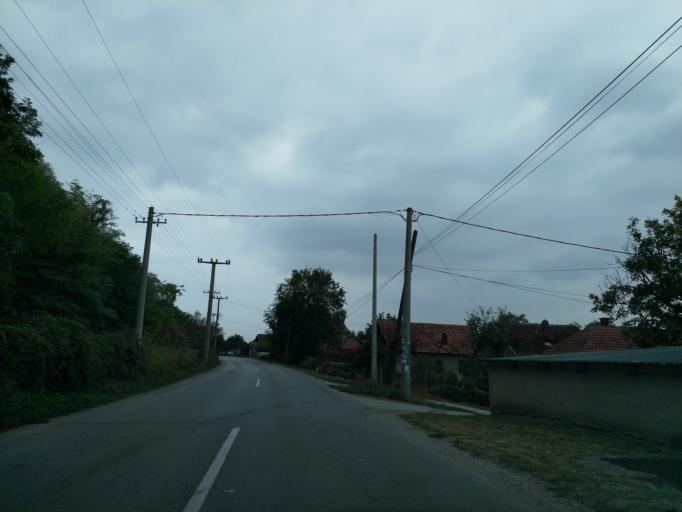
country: RS
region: Central Serbia
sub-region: Sumadijski Okrug
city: Batocina
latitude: 44.1041
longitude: 21.1617
